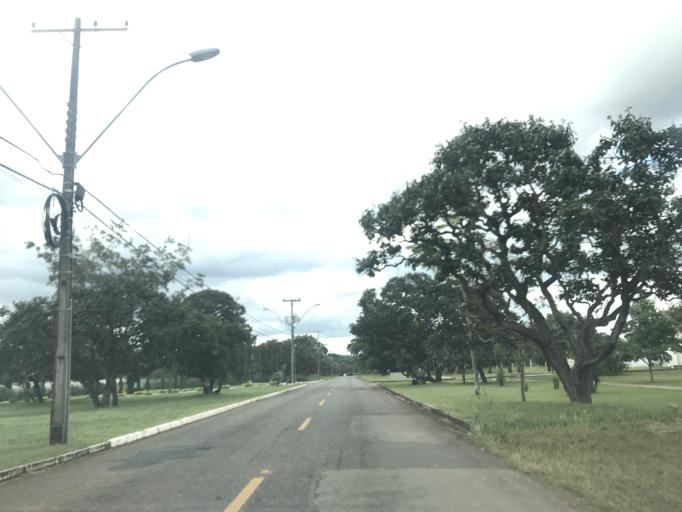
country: BR
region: Federal District
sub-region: Brasilia
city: Brasilia
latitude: -15.9013
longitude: -47.9390
